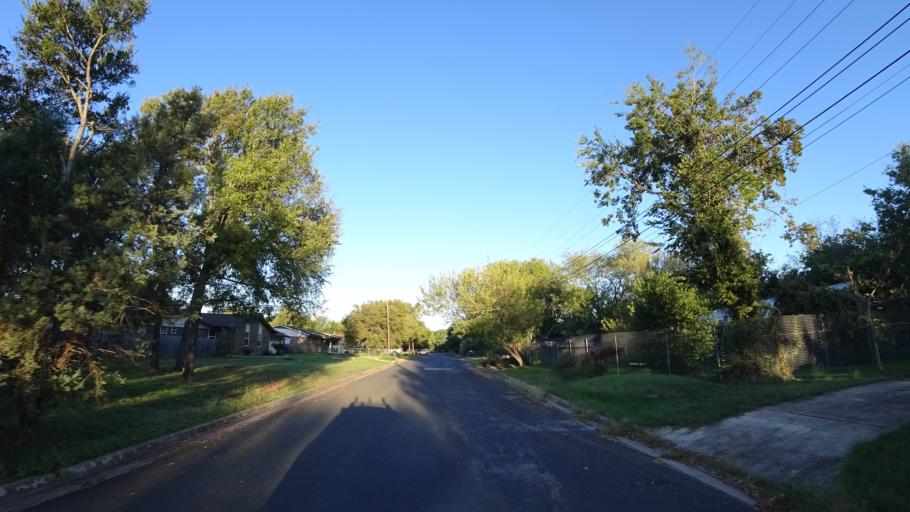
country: US
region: Texas
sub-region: Travis County
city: Austin
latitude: 30.2897
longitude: -97.6813
